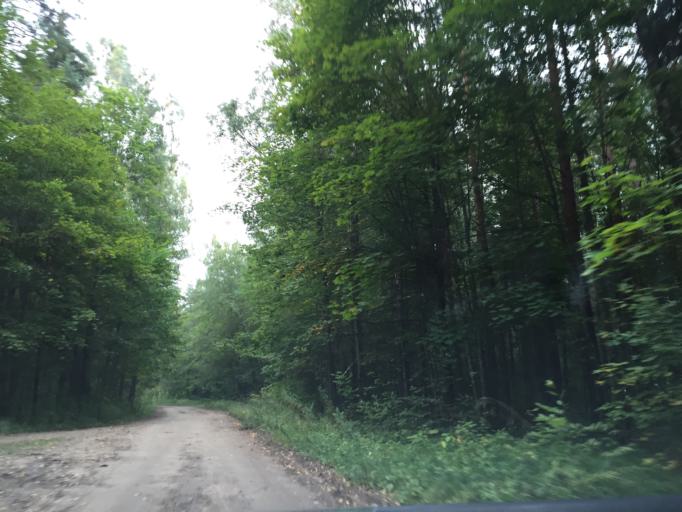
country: LV
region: Ogre
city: Ogre
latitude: 56.8215
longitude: 24.6579
